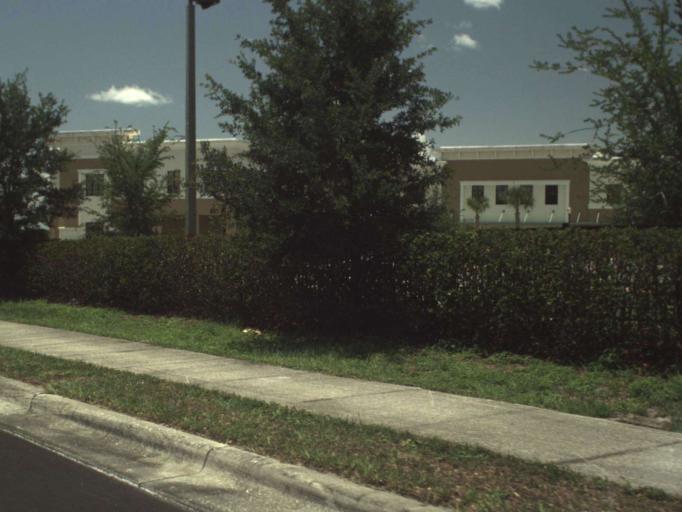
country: US
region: Florida
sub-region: Seminole County
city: Winter Springs
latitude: 28.7049
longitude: -81.2711
